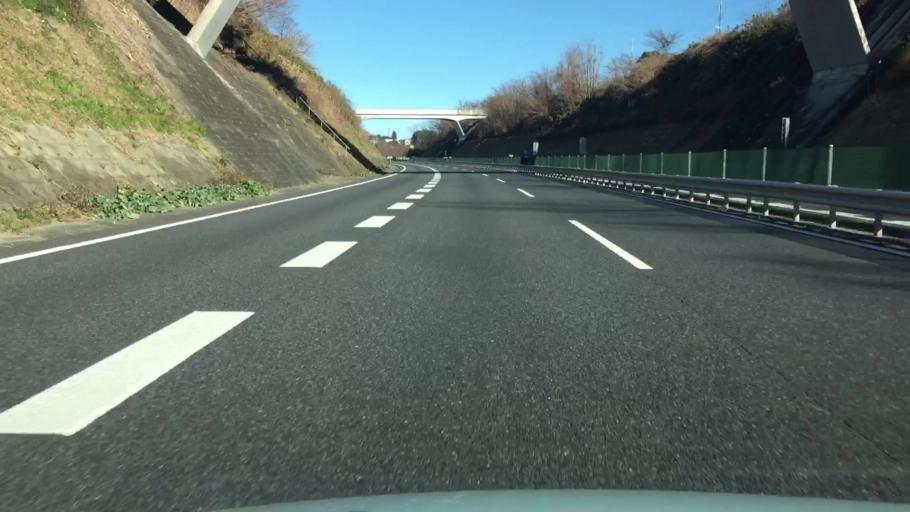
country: JP
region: Gunma
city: Shibukawa
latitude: 36.4871
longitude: 139.0294
